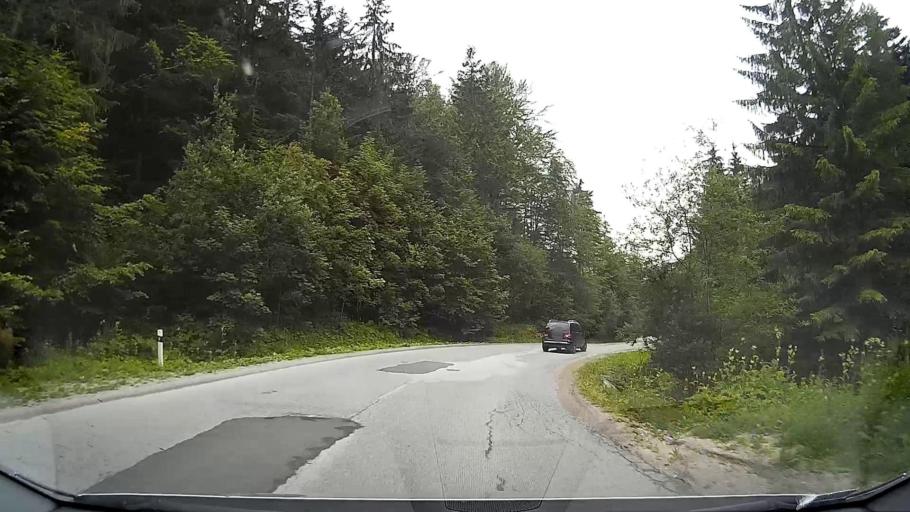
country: SK
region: Banskobystricky
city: Revuca
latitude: 48.7882
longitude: 20.1301
